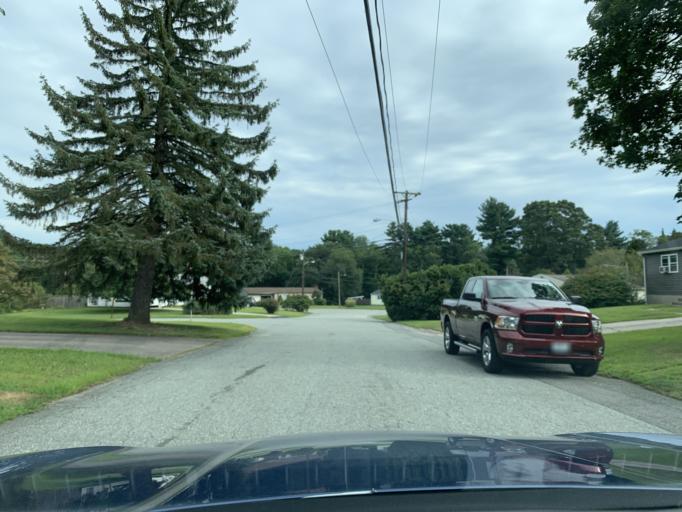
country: US
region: Rhode Island
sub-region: Kent County
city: East Greenwich
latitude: 41.6208
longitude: -71.4559
